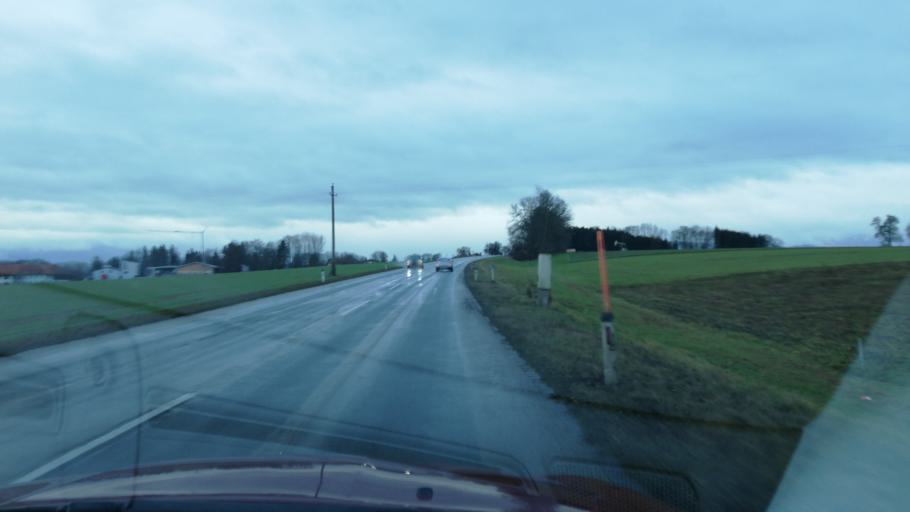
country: AT
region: Upper Austria
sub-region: Wels-Land
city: Sattledt
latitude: 48.0234
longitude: 14.0597
